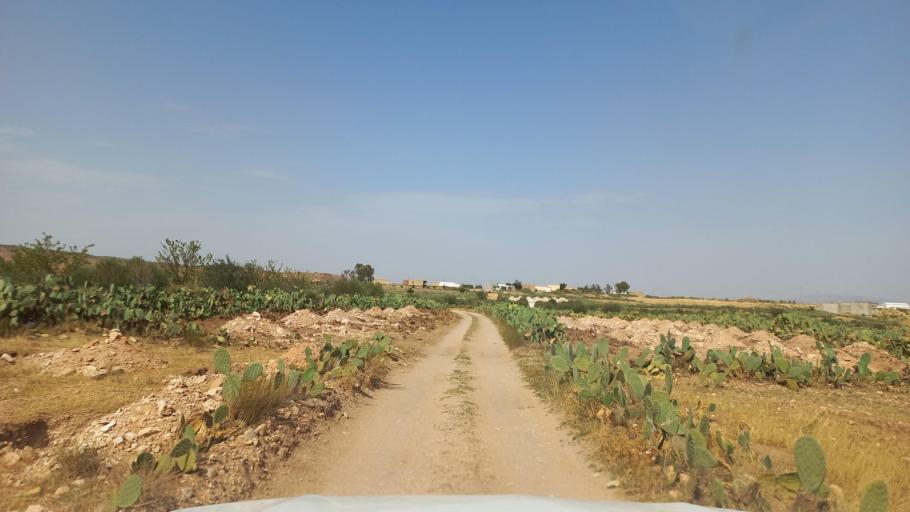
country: TN
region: Al Qasrayn
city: Kasserine
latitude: 35.2956
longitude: 8.9471
